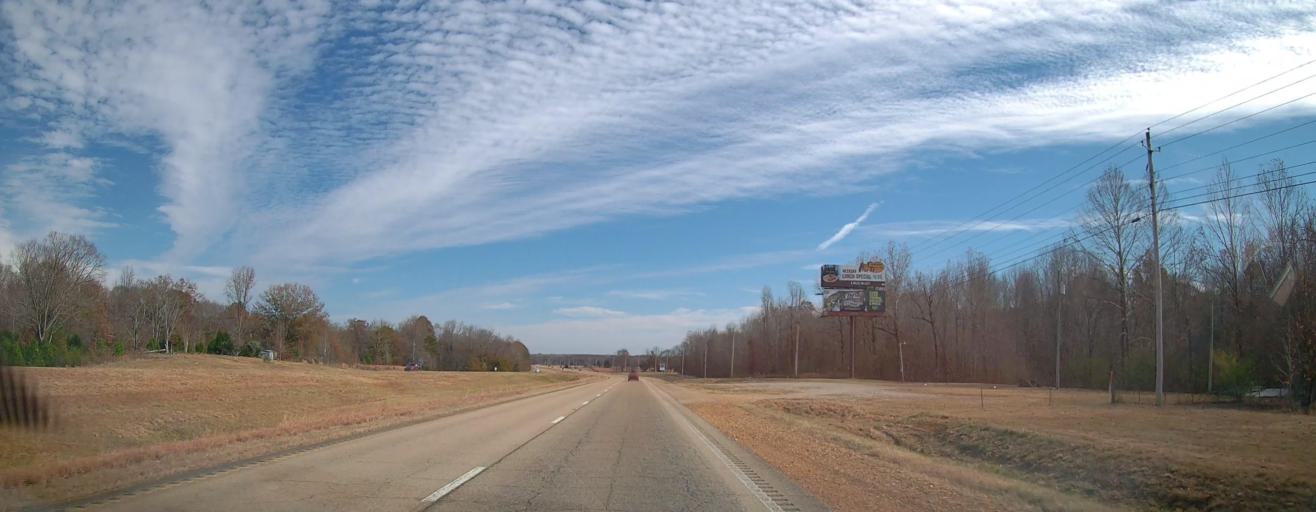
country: US
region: Mississippi
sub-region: Alcorn County
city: Corinth
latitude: 34.9316
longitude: -88.6428
